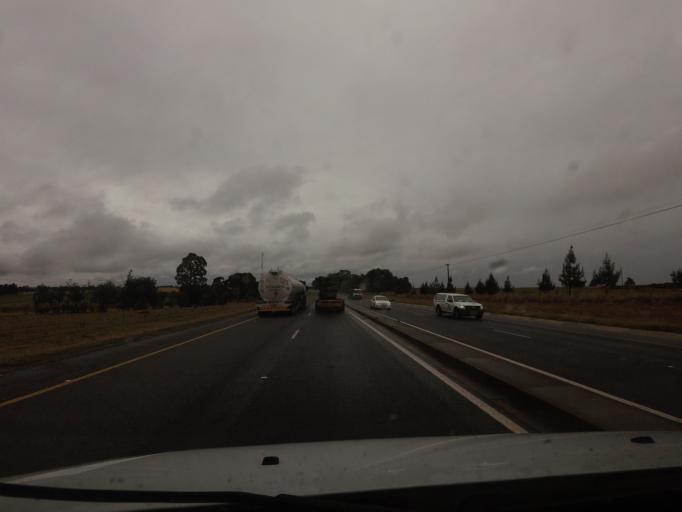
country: ZA
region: Mpumalanga
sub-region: Nkangala District Municipality
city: Belfast
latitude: -25.7485
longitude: 30.0013
